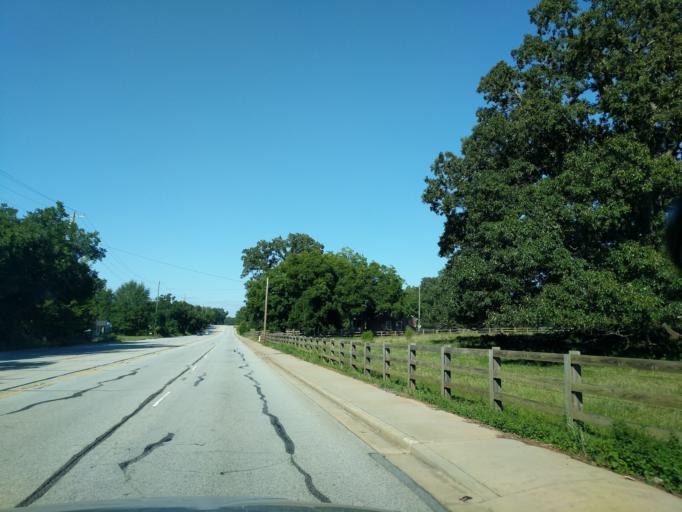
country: US
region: South Carolina
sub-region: Laurens County
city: Clinton
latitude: 34.4899
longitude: -81.8515
